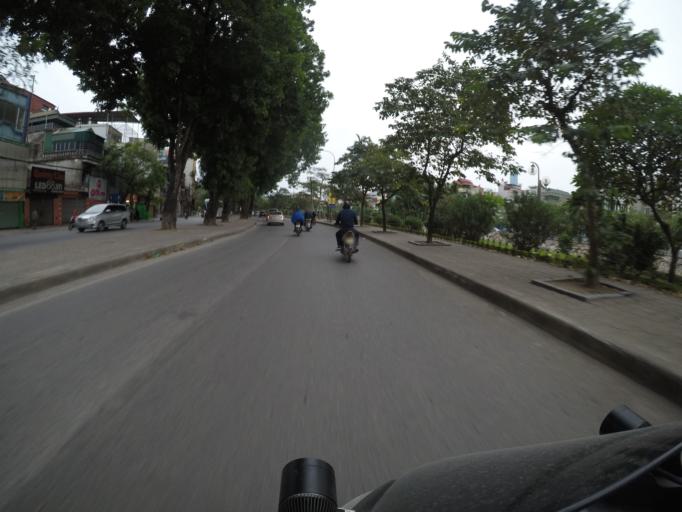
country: VN
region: Ha Noi
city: Cau Giay
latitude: 21.0256
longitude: 105.7982
